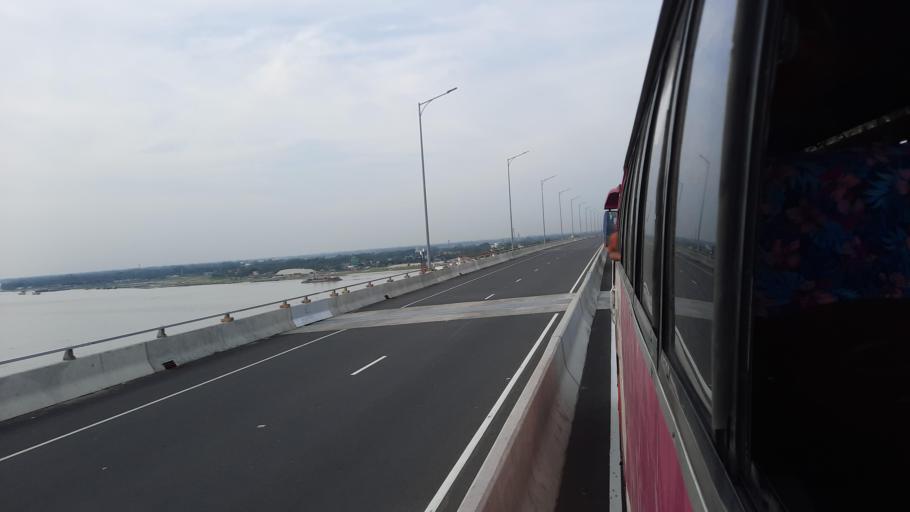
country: BD
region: Dhaka
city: Char Bhadrasan
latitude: 23.4625
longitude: 90.2630
